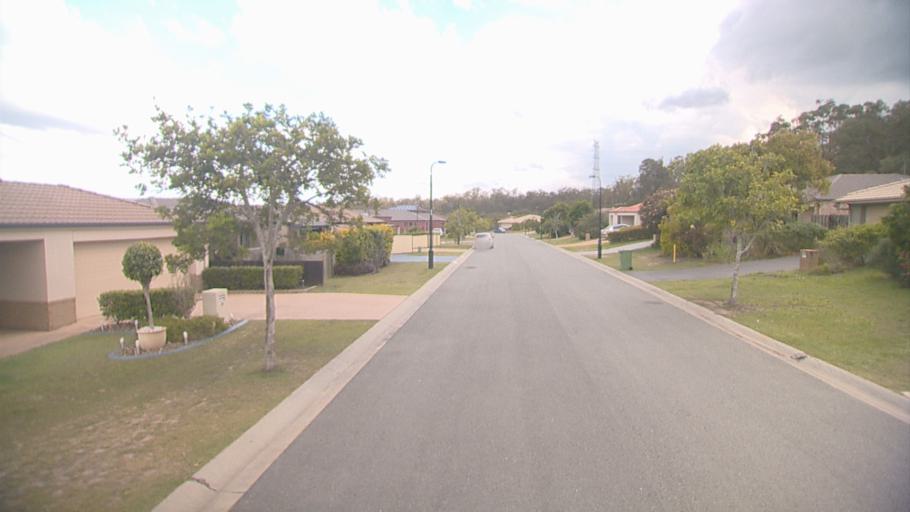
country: AU
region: Queensland
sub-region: Logan
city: Woodridge
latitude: -27.6560
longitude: 153.0742
